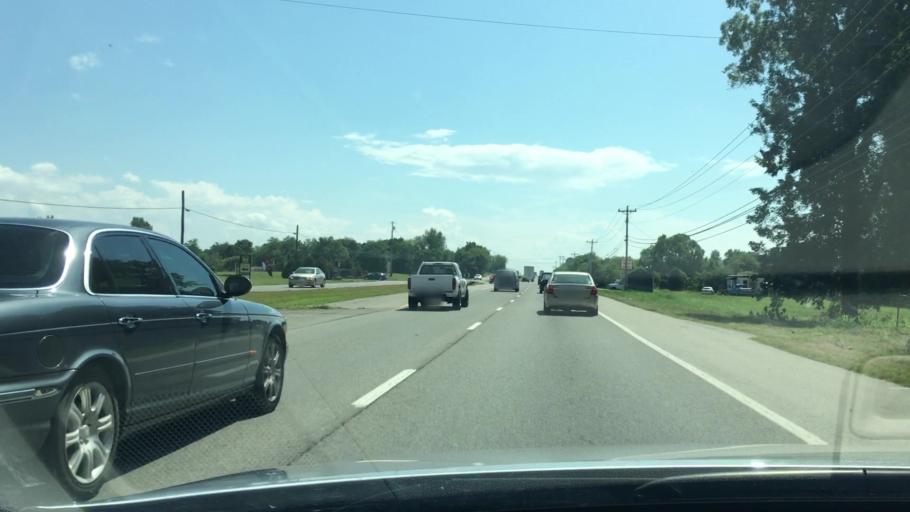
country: US
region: Tennessee
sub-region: Maury County
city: Spring Hill
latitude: 35.6939
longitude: -86.9887
